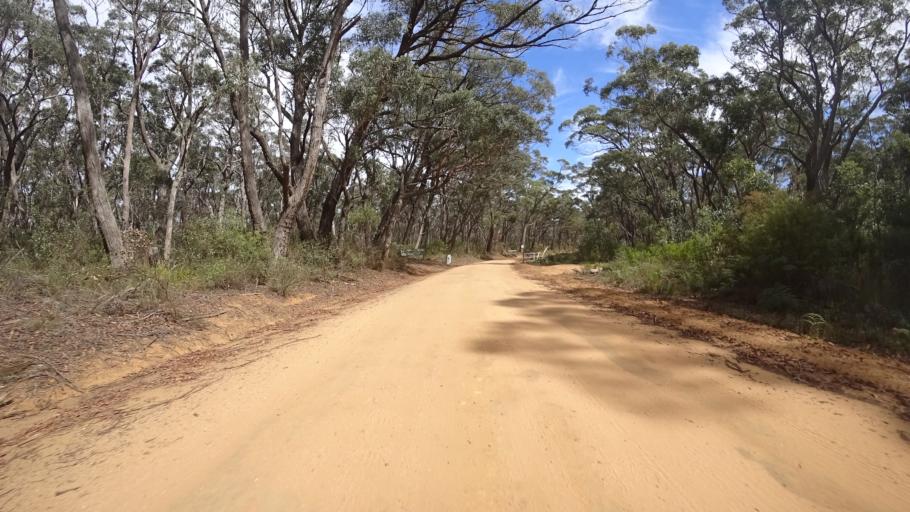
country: AU
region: New South Wales
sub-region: Lithgow
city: Lithgow
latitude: -33.3162
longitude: 150.2417
